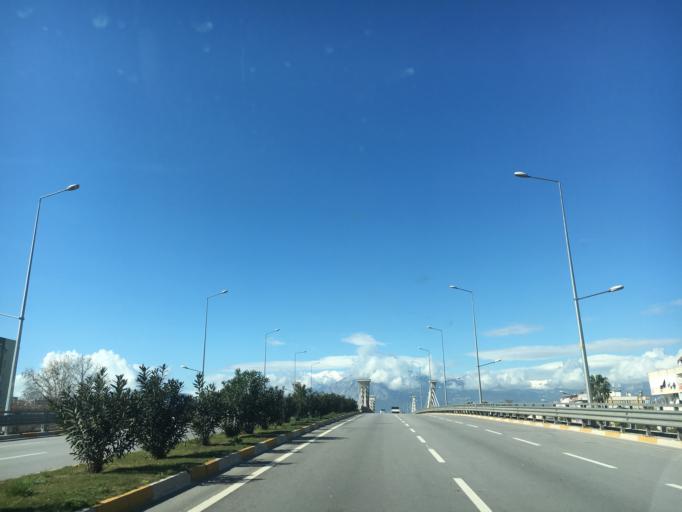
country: TR
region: Antalya
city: Antalya
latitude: 36.9069
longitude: 30.6843
